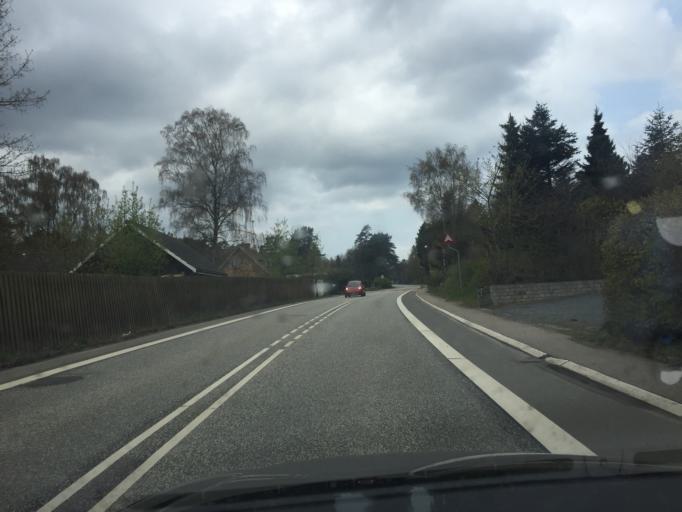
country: DK
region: Capital Region
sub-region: Halsnaes Kommune
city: Frederiksvaerk
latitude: 56.0045
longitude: 12.0035
